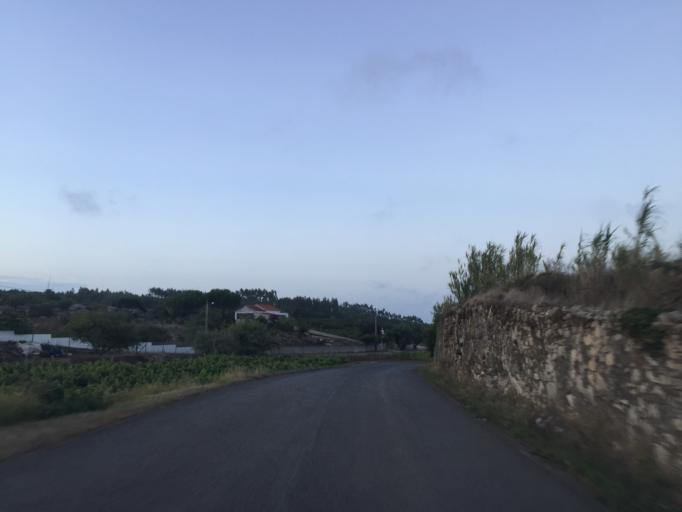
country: PT
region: Leiria
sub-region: Bombarral
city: Bombarral
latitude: 39.2915
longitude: -9.2089
